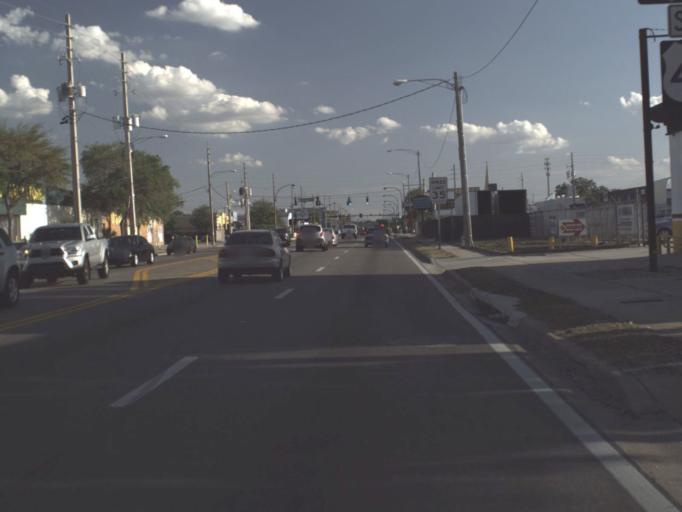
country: US
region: Florida
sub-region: Orange County
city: Orlando
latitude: 28.5435
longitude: -81.3974
